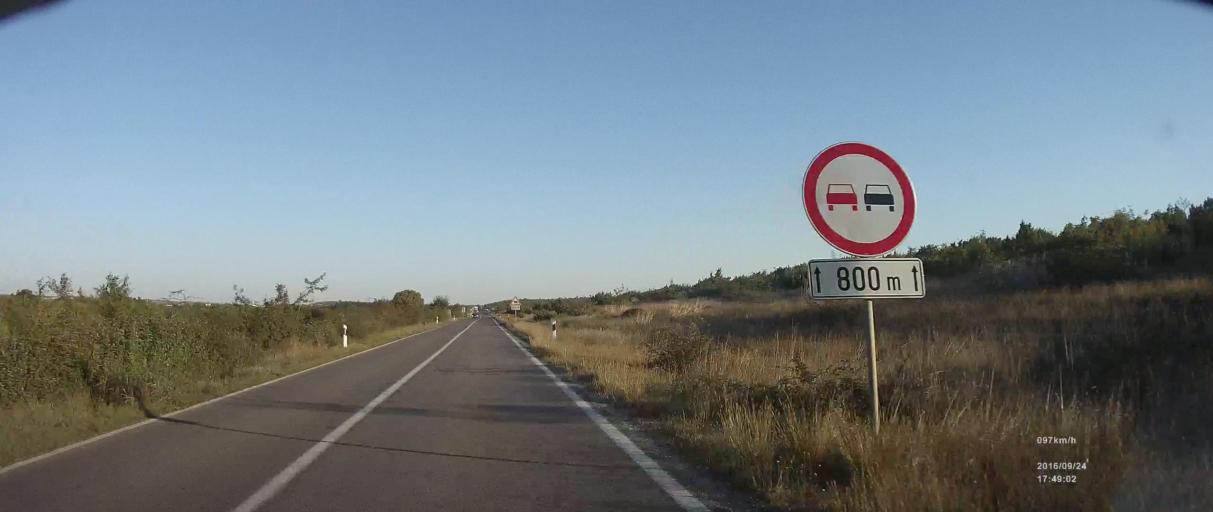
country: HR
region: Zadarska
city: Polaca
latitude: 44.0583
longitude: 15.5444
